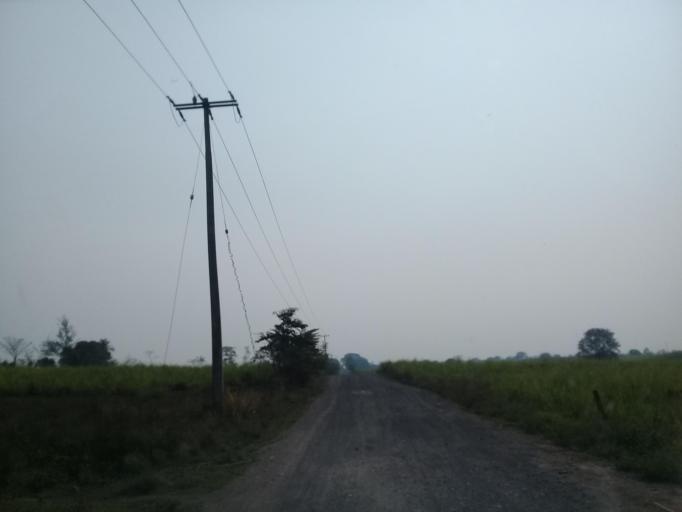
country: MX
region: Oaxaca
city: Acatlan de Perez Figueroa
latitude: 18.6076
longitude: -96.5737
